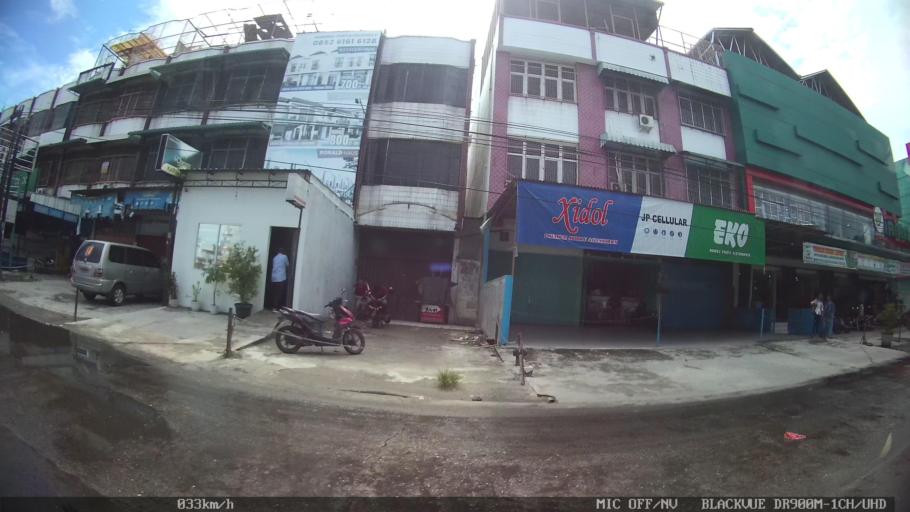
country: ID
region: North Sumatra
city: Medan
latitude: 3.5967
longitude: 98.7066
